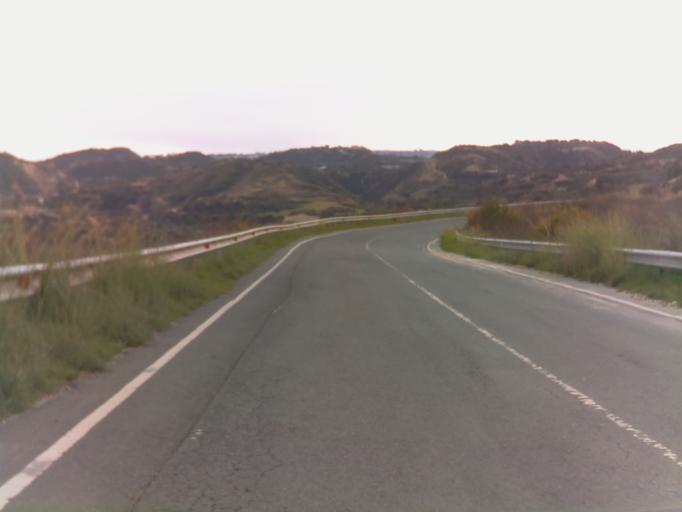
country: CY
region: Pafos
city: Polis
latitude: 35.0166
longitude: 32.4104
